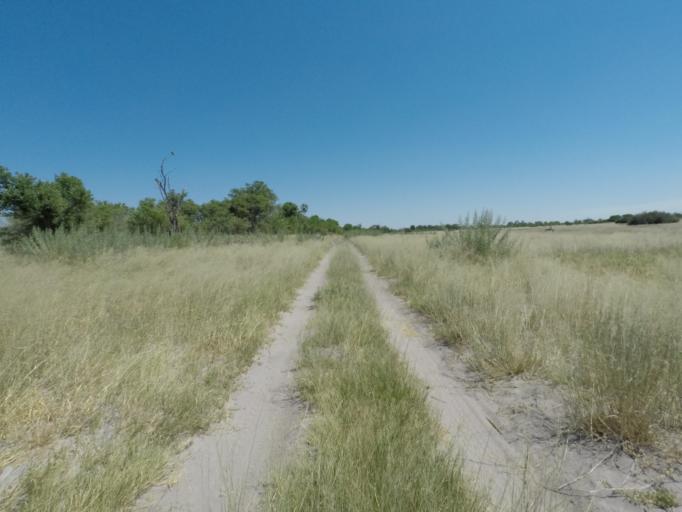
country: BW
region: North West
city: Maun
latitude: -19.4762
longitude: 23.5523
